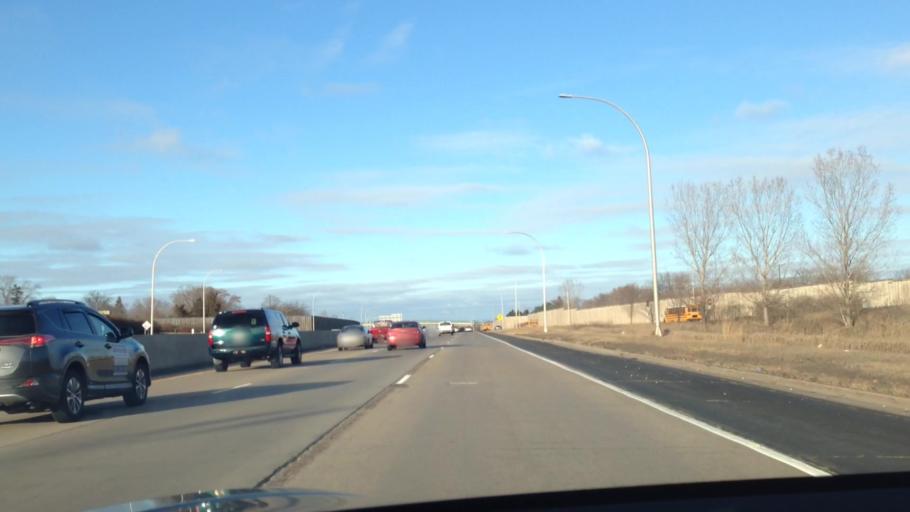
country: US
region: Minnesota
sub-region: Hennepin County
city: Golden Valley
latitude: 45.0216
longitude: -93.3484
